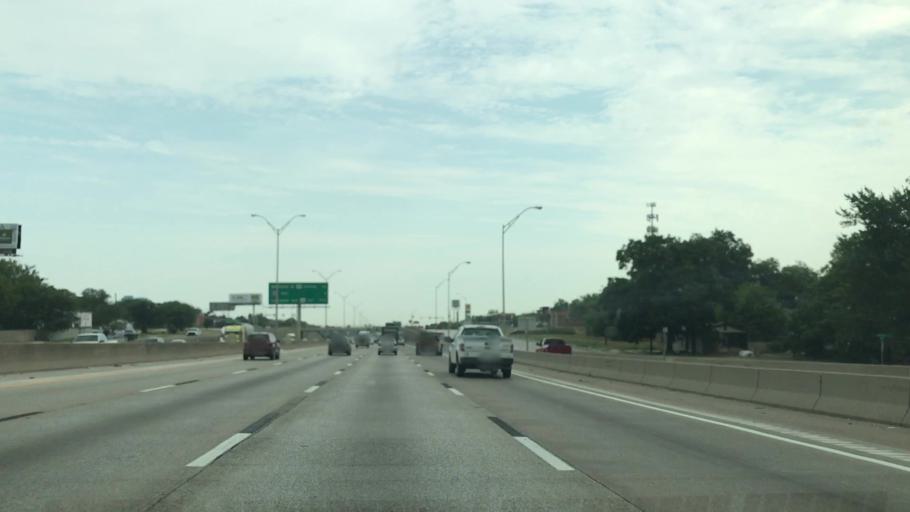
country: US
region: Texas
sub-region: Tarrant County
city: Fort Worth
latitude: 32.7225
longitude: -97.3204
